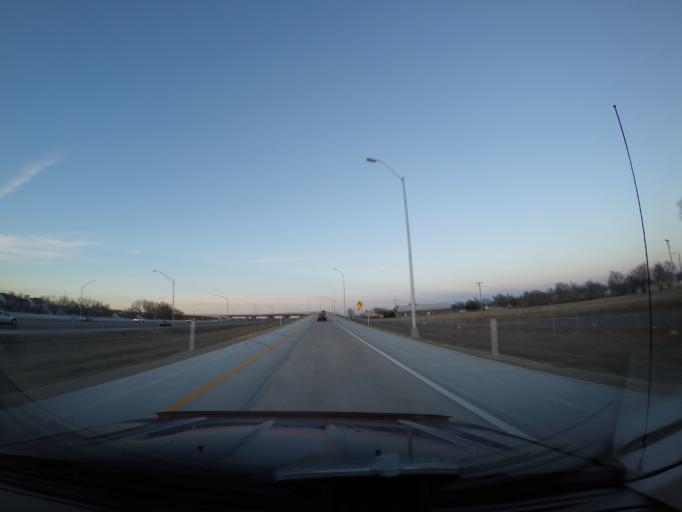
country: US
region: Kansas
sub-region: Sedgwick County
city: Wichita
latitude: 37.7034
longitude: -97.4087
